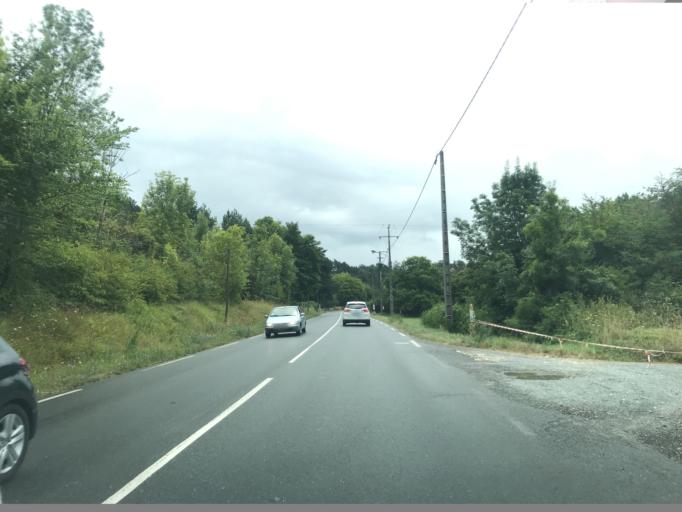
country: FR
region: Aquitaine
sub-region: Departement de la Dordogne
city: Chancelade
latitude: 45.2383
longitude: 0.6853
